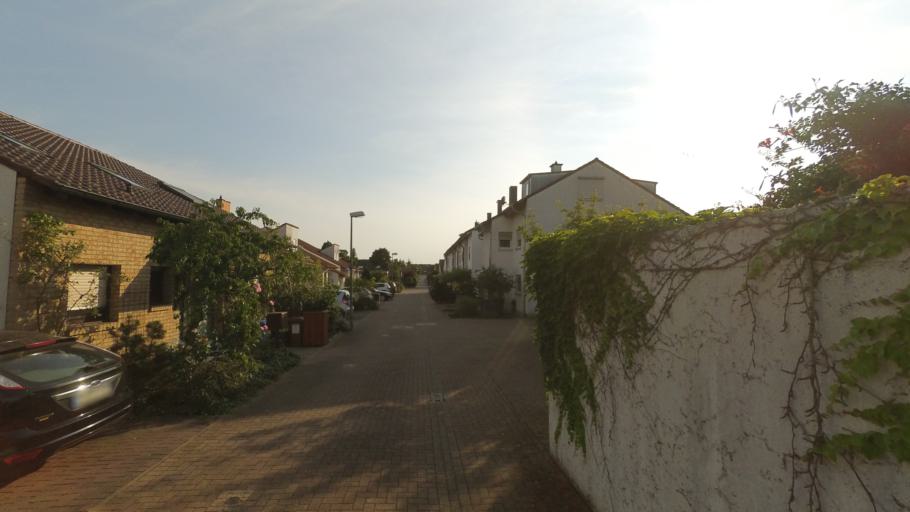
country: DE
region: Rheinland-Pfalz
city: Gartenstadt
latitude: 49.4535
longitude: 8.4006
